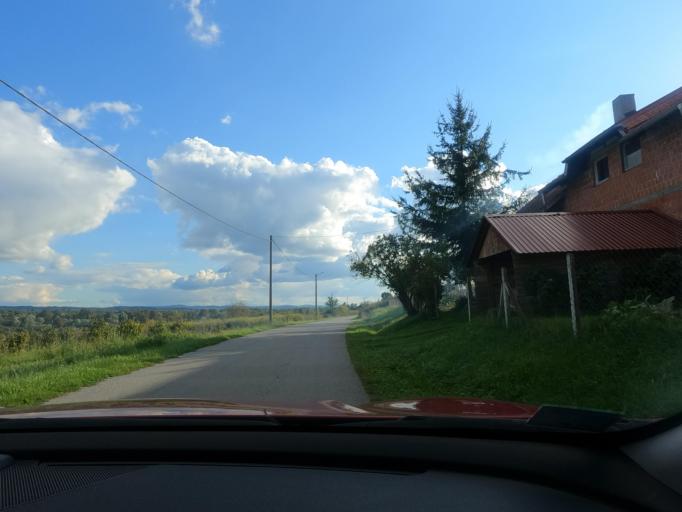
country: HR
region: Sisacko-Moslavacka
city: Petrinja
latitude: 45.3789
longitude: 16.2416
